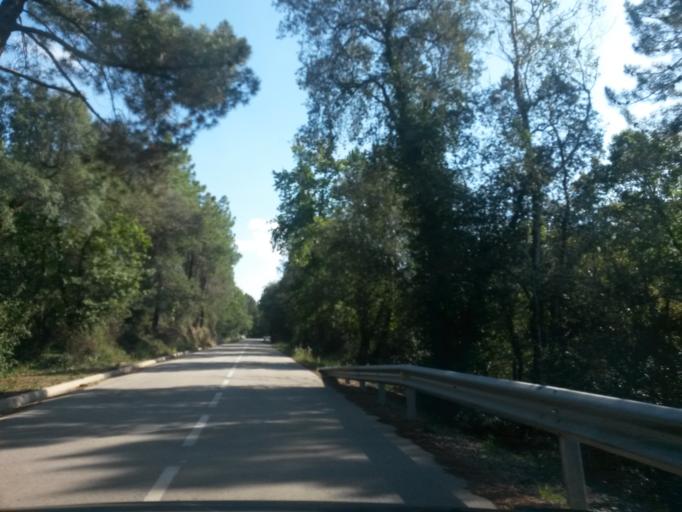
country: ES
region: Catalonia
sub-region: Provincia de Girona
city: Bescano
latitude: 41.9507
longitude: 2.6997
